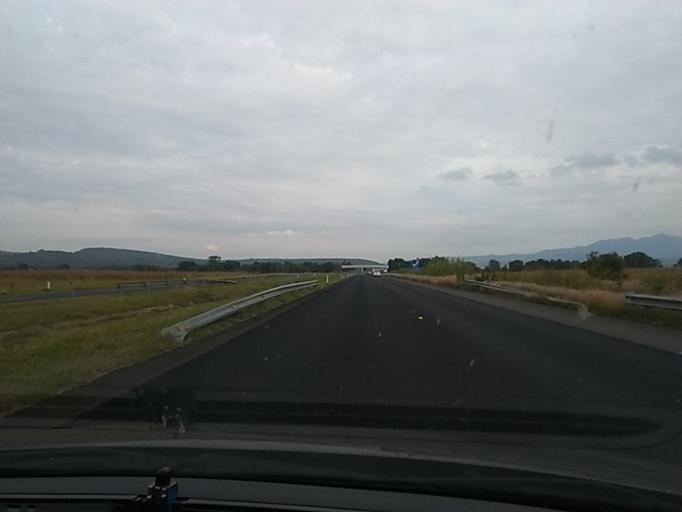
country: MX
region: Michoacan
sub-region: Jimenez
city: Copandaro (Copandaro del Cuatro)
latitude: 19.9189
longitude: -101.5951
